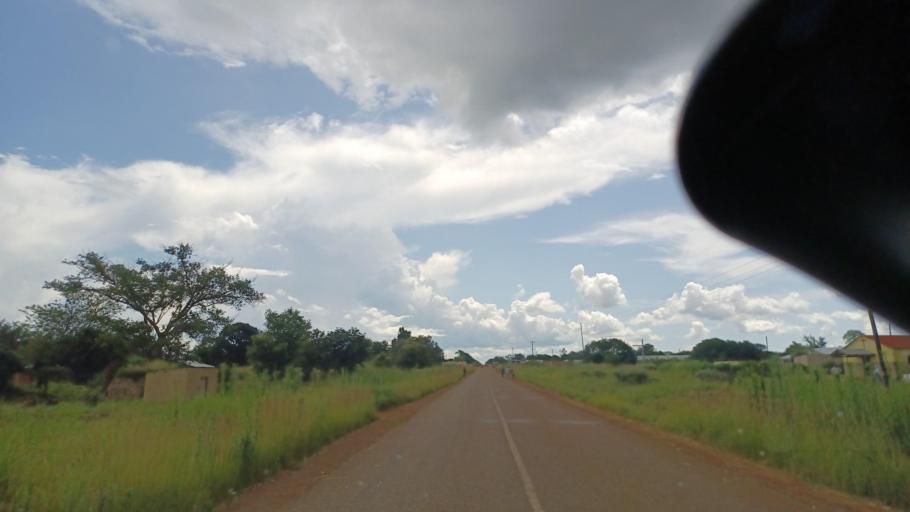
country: ZM
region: North-Western
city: Kasempa
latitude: -13.1040
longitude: 25.8743
